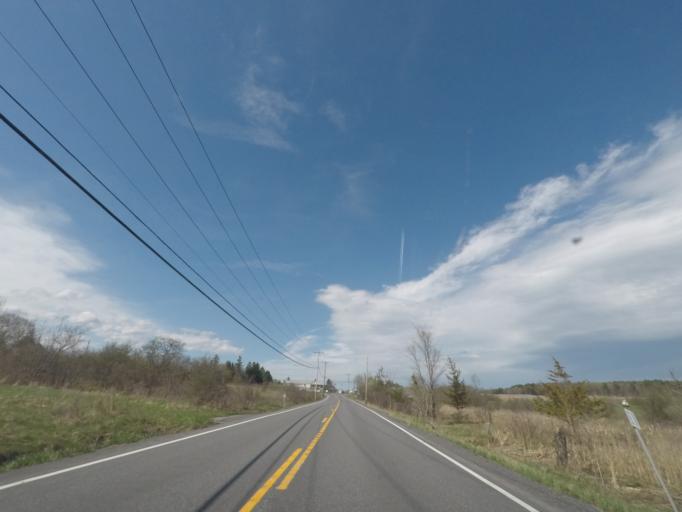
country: US
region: New York
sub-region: Greene County
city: Cairo
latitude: 42.4407
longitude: -74.0167
